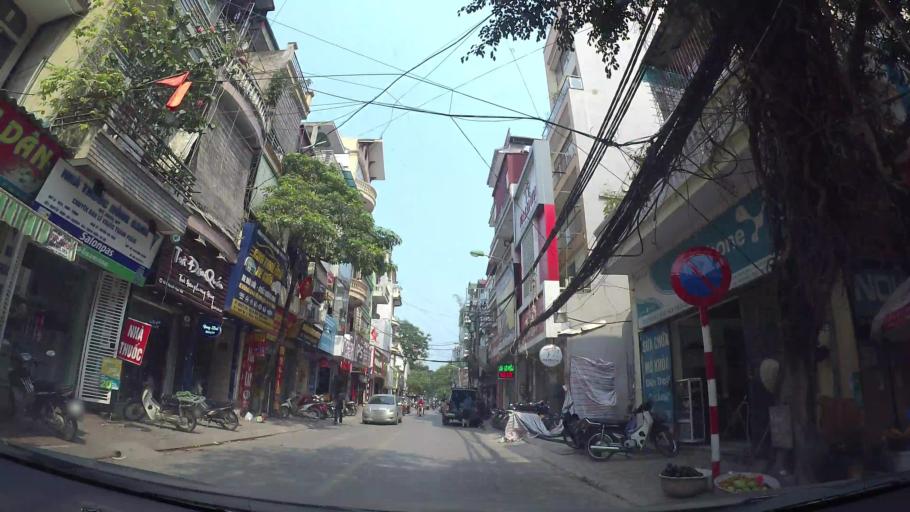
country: VN
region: Ha Noi
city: Dong Da
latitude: 21.0004
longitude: 105.8224
